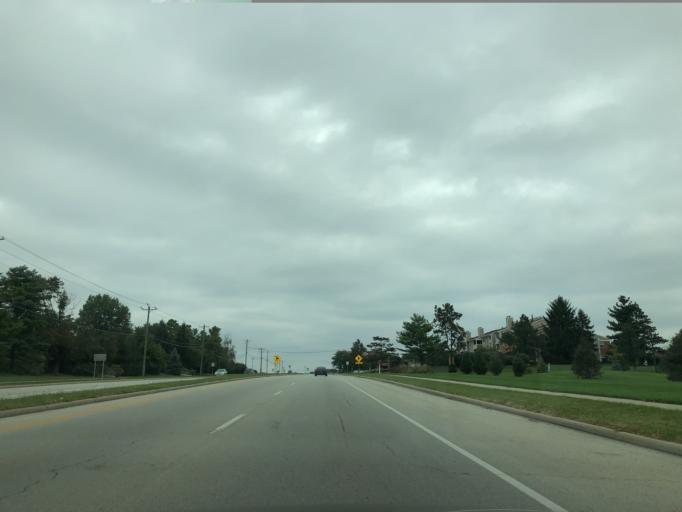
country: US
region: Ohio
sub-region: Warren County
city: Landen
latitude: 39.2962
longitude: -84.2917
